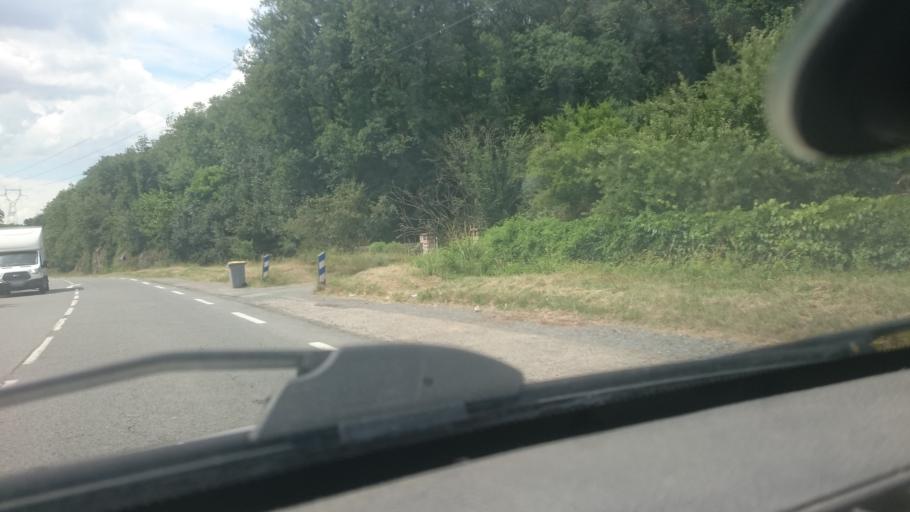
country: FR
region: Rhone-Alpes
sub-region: Departement du Rhone
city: Lozanne
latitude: 45.8568
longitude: 4.6628
